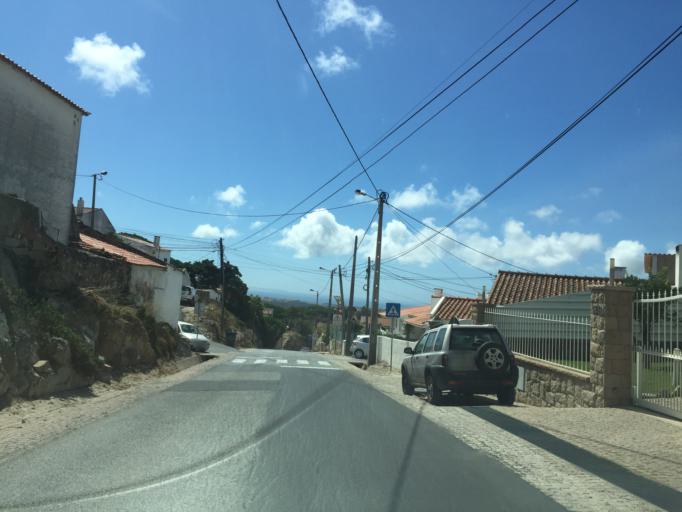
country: PT
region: Lisbon
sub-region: Cascais
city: Alcabideche
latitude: 38.7555
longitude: -9.4469
